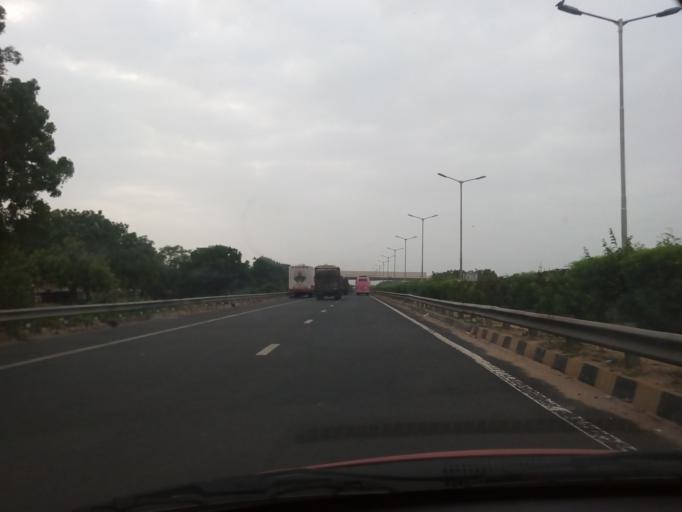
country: IN
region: Gujarat
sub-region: Ahmadabad
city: Ahmedabad
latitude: 22.9745
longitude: 72.6526
